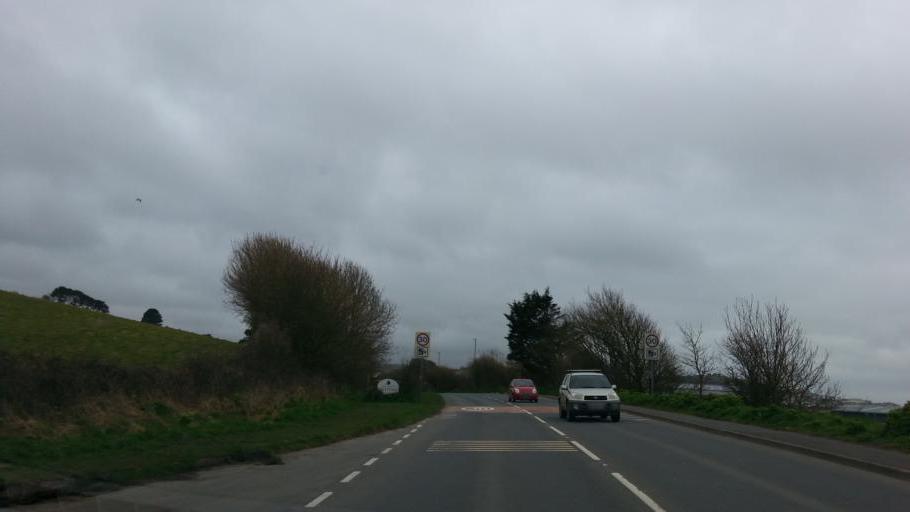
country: GB
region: England
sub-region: Devon
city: Appledore
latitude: 51.0599
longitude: -4.1725
